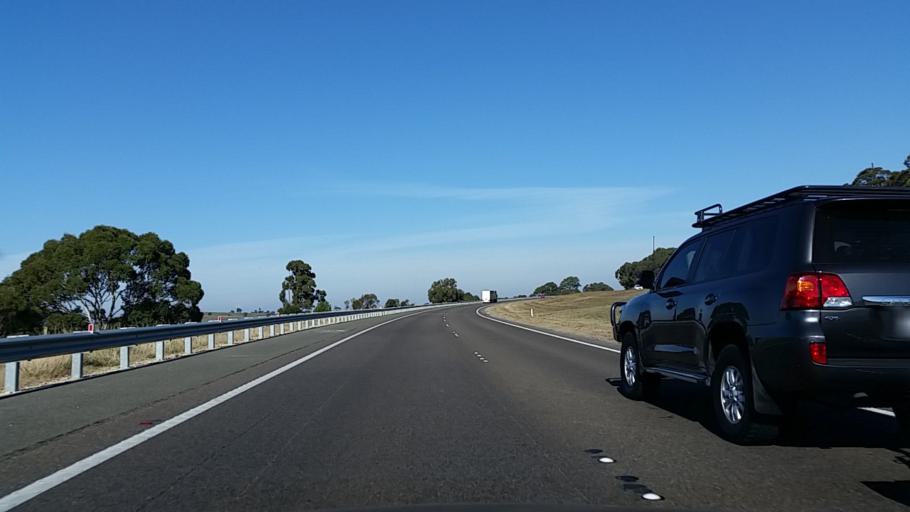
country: AU
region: South Australia
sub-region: Mount Barker
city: Nairne
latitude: -35.0865
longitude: 138.9601
